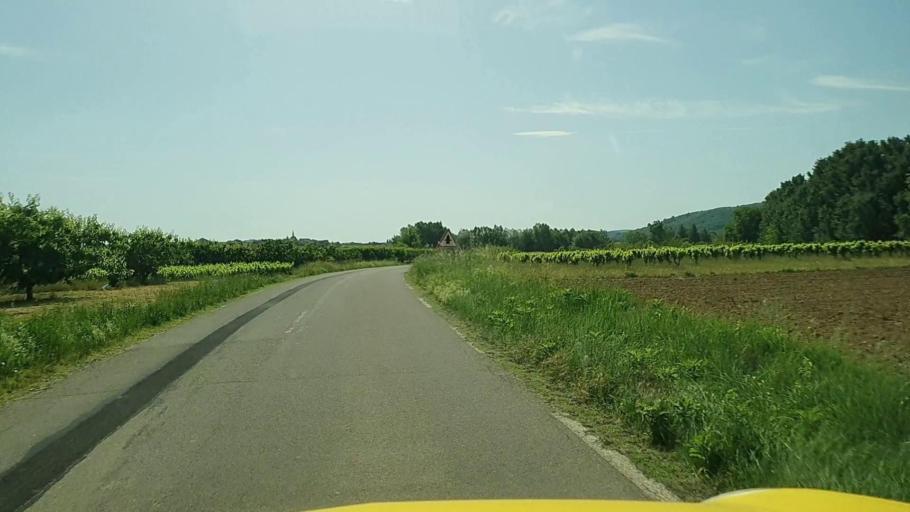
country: FR
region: Languedoc-Roussillon
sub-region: Departement du Gard
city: Sabran
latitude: 44.1054
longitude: 4.5403
